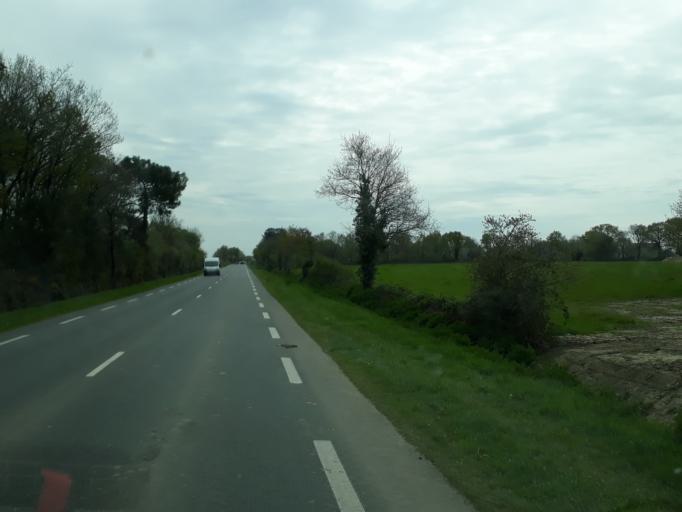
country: FR
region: Brittany
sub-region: Departement du Morbihan
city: Ferel
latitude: 47.5231
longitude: -2.3772
